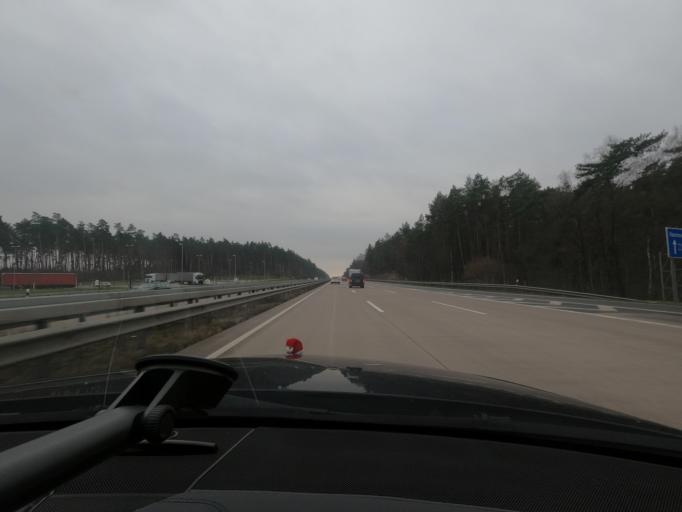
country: DE
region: Lower Saxony
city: Bad Fallingbostel
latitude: 52.8101
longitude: 9.6797
